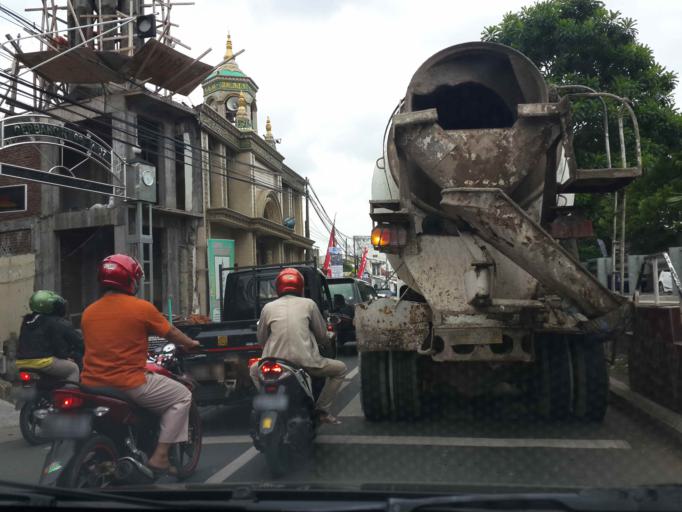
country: ID
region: East Java
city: Gubengairlangga
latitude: -7.2704
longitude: 112.7199
